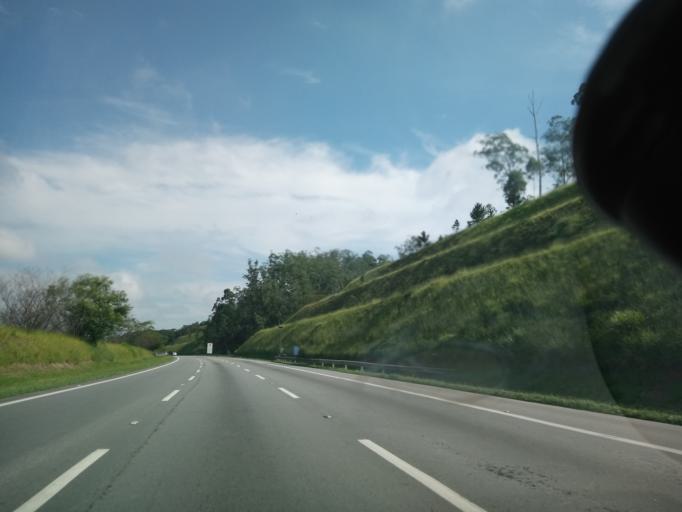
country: BR
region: Sao Paulo
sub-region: Itapecerica Da Serra
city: Itapecerica da Serra
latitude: -23.6841
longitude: -46.8190
